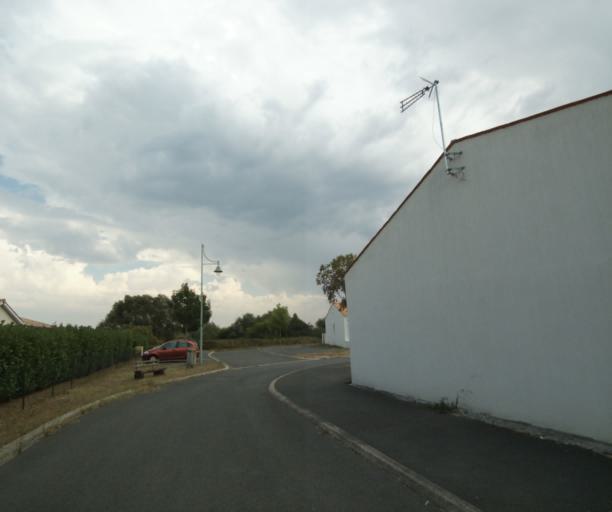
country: FR
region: Poitou-Charentes
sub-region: Departement de la Charente-Maritime
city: Tonnay-Charente
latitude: 45.9478
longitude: -0.9005
